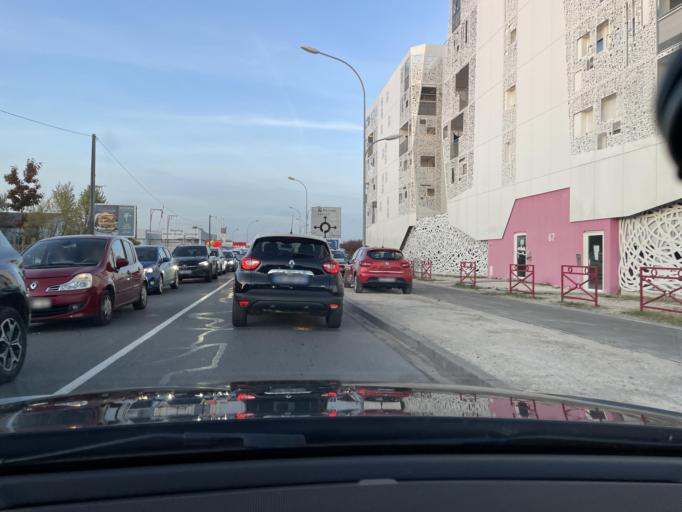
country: FR
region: Aquitaine
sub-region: Departement de la Gironde
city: Villenave-d'Ornon
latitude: 44.7874
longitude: -0.5362
